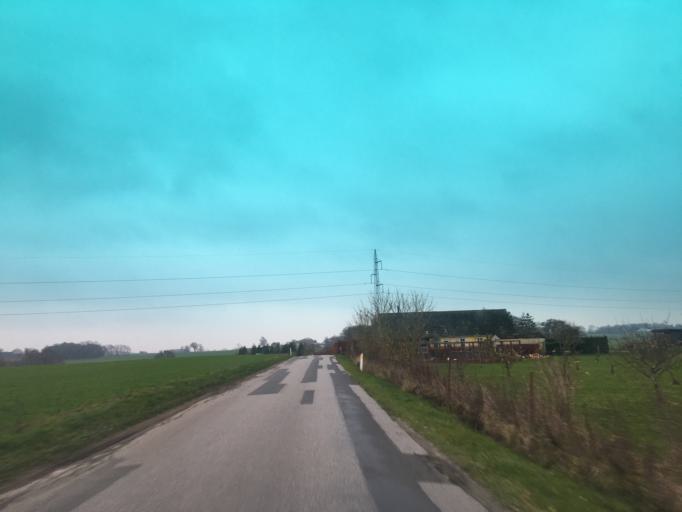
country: DK
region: Zealand
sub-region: Slagelse Kommune
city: Skaelskor
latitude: 55.2338
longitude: 11.4228
